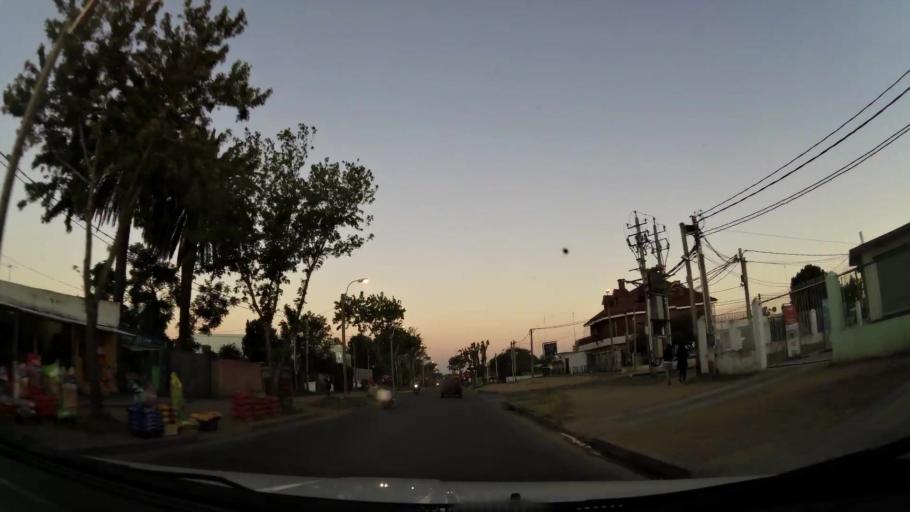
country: UY
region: Canelones
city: Toledo
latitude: -34.8173
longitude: -56.1416
